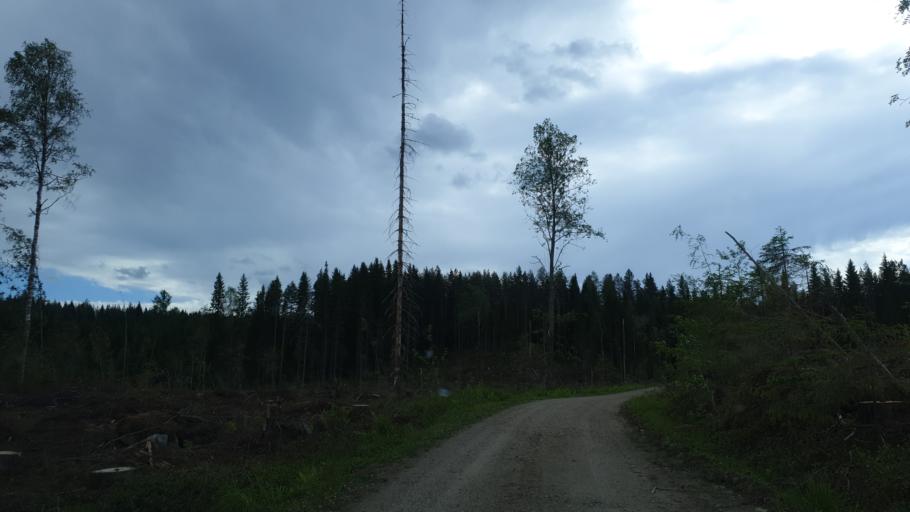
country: FI
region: Northern Savo
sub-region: Koillis-Savo
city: Kaavi
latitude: 62.9801
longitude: 28.7565
